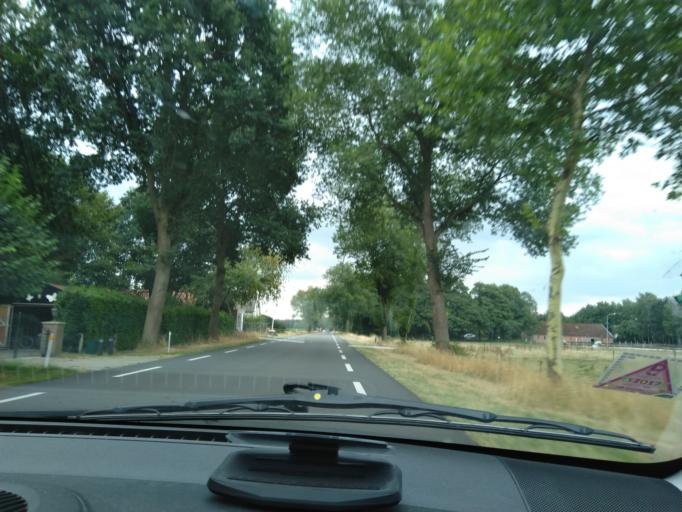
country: DE
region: Lower Saxony
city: Rhede
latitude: 53.0762
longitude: 7.1903
